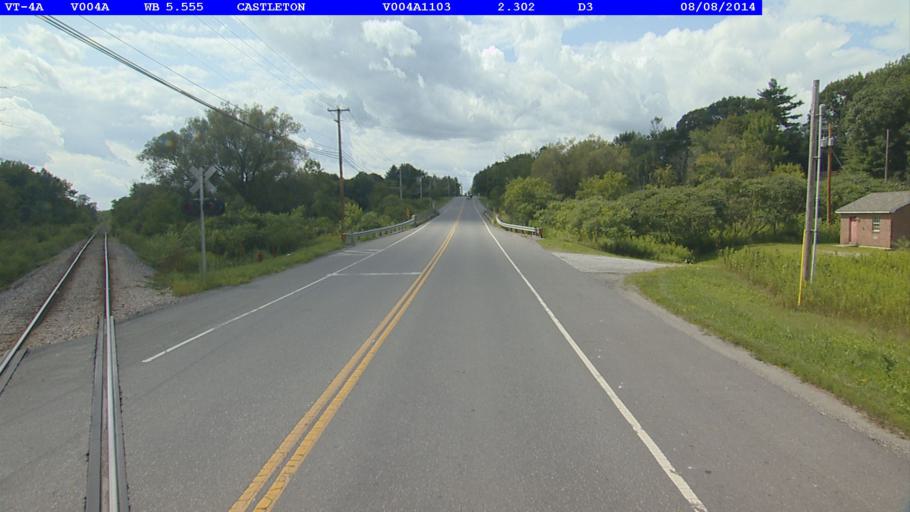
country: US
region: Vermont
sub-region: Rutland County
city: Castleton
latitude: 43.6073
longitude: -73.1990
